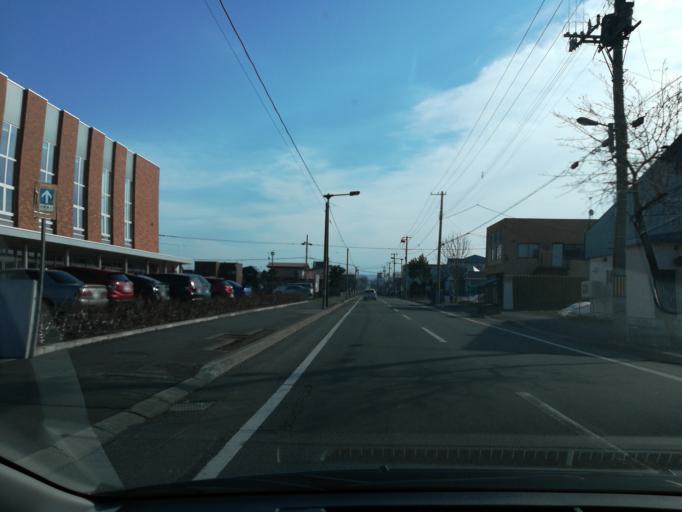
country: JP
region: Hokkaido
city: Iwamizawa
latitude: 43.2075
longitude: 141.7705
